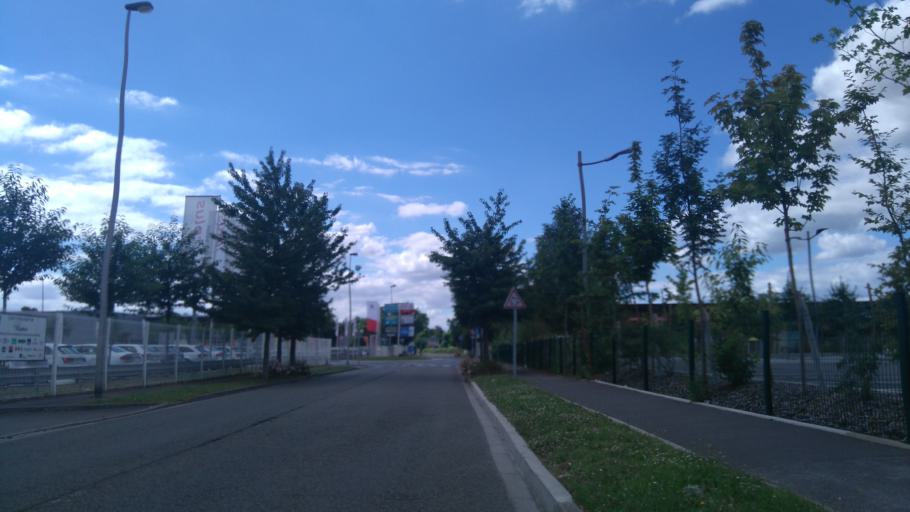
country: FR
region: Picardie
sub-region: Departement de l'Oise
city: Saint-Maximin
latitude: 49.2328
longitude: 2.4631
